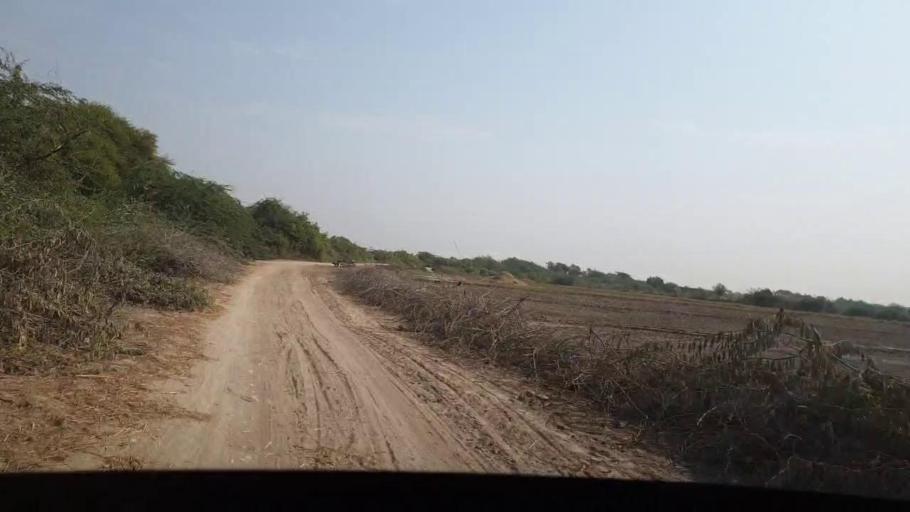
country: PK
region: Sindh
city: Chuhar Jamali
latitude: 24.2694
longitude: 67.9218
